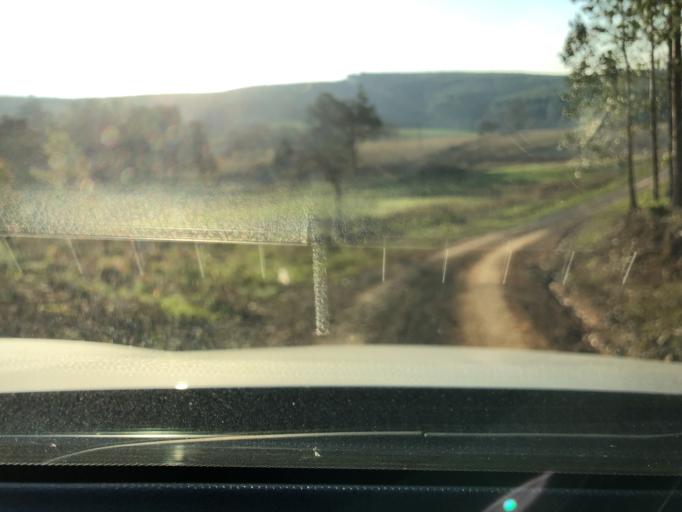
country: ZA
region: KwaZulu-Natal
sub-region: Sisonke District Municipality
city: Ixopo
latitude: -30.1822
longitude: 30.0492
